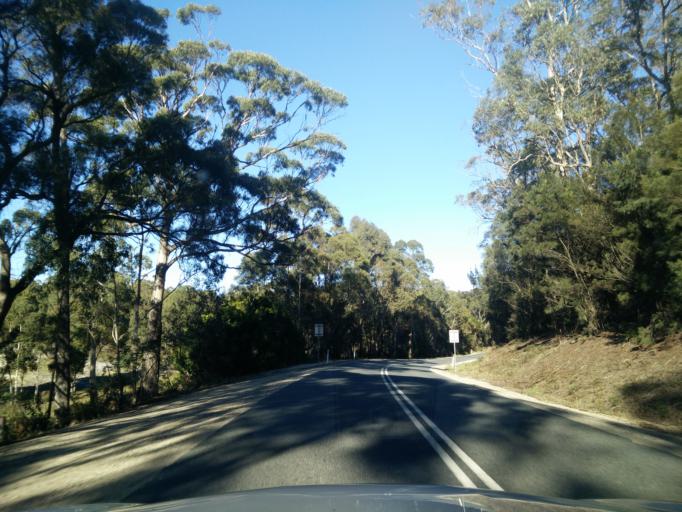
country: AU
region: Tasmania
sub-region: Break O'Day
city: St Helens
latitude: -41.8872
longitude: 148.2968
